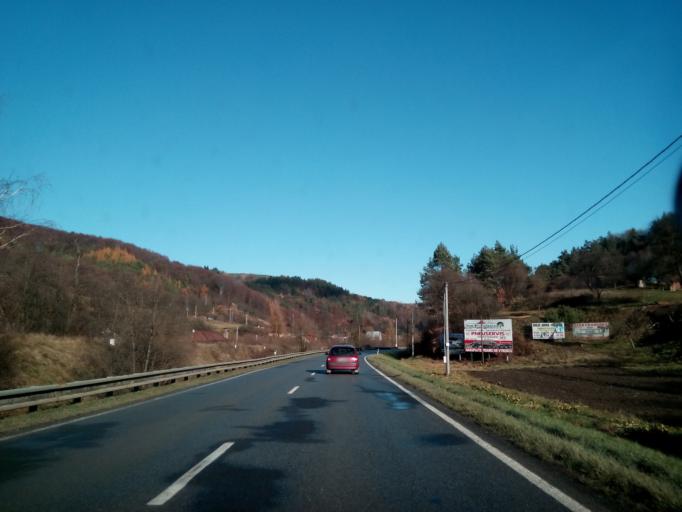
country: SK
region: Presovsky
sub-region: Okres Bardejov
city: Bardejov
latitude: 49.2626
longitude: 21.2518
